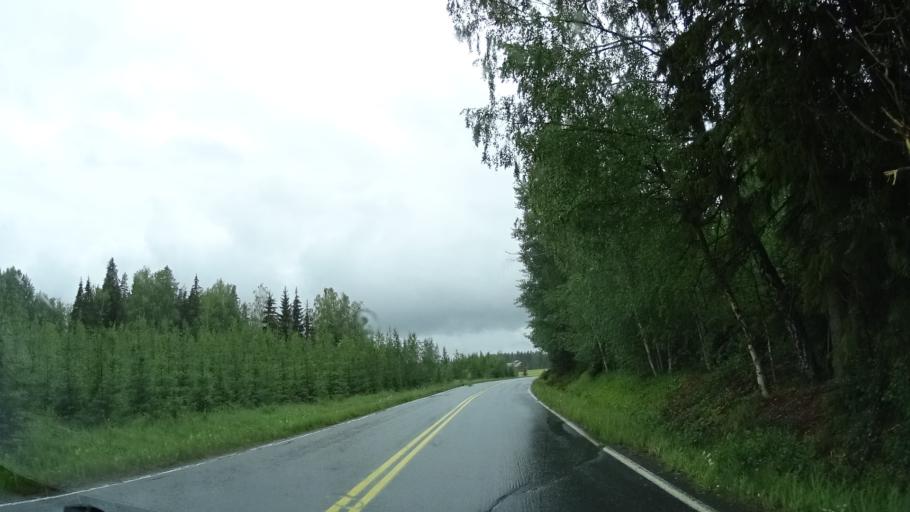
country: FI
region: Haeme
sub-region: Forssa
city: Humppila
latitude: 60.9929
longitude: 23.2558
